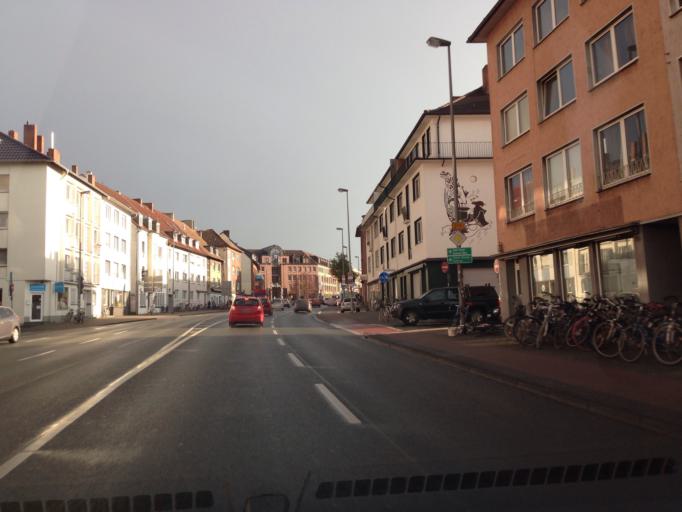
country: DE
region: North Rhine-Westphalia
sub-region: Regierungsbezirk Munster
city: Muenster
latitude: 51.9543
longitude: 7.6198
